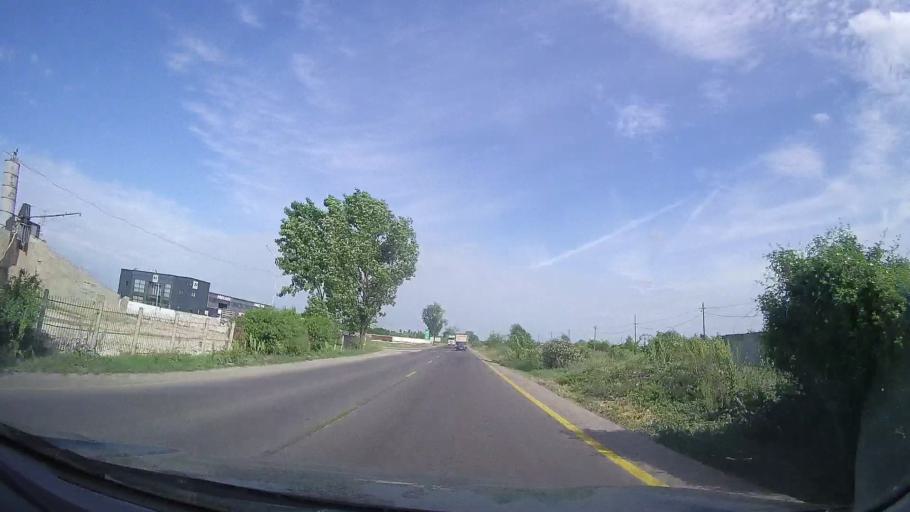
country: RO
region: Ilfov
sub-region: Comuna Magurele
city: Varteju
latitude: 44.3702
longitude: 26.0122
